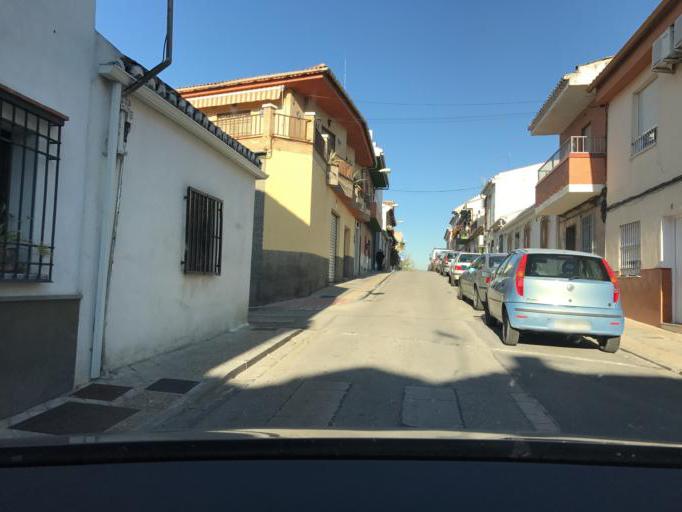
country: ES
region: Andalusia
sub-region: Provincia de Granada
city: Maracena
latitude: 37.2010
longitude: -3.6274
